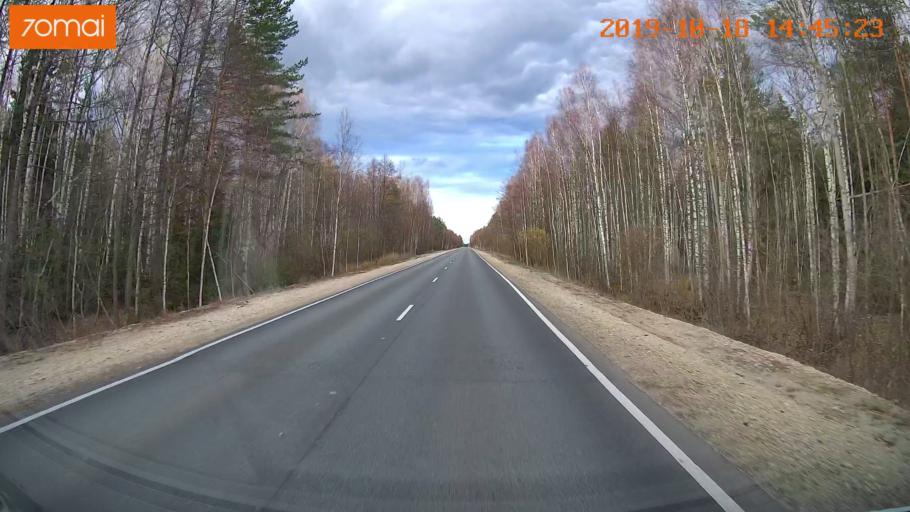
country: RU
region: Vladimir
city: Velikodvorskiy
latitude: 55.3540
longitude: 40.6788
